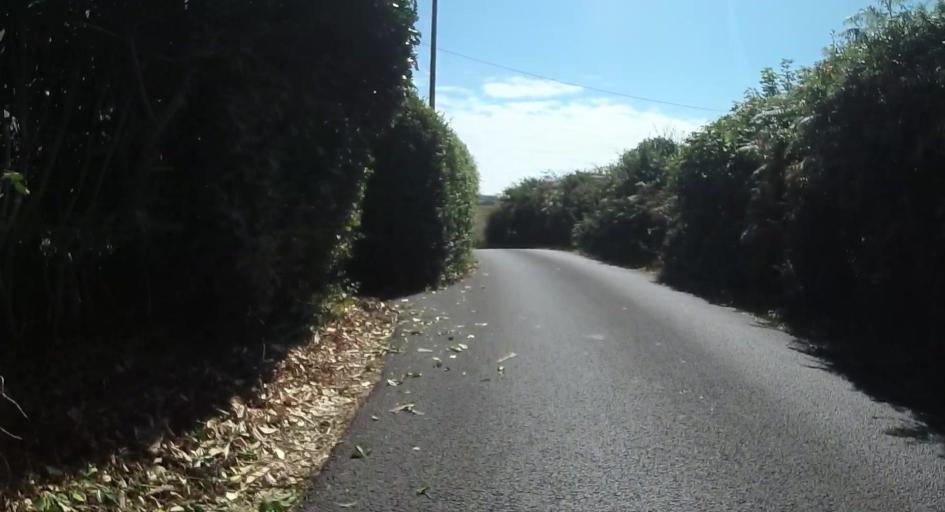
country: GB
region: England
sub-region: Isle of Wight
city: Chale
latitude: 50.6040
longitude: -1.3305
